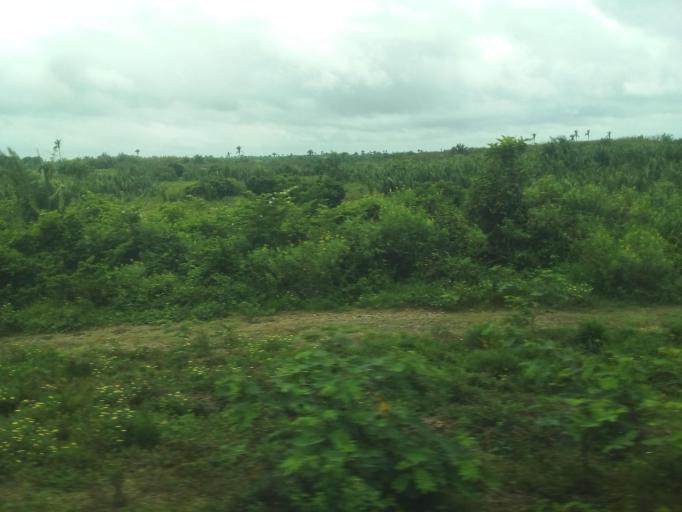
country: BR
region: Maranhao
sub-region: Moncao
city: Moncao
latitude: -3.5824
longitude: -45.0581
